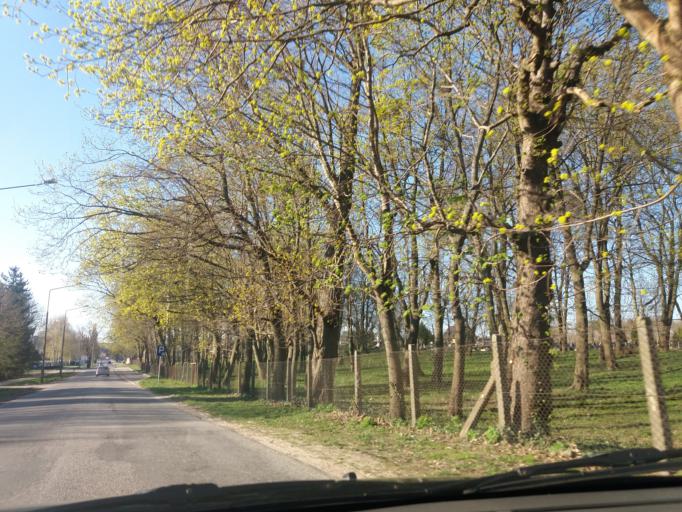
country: PL
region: Warmian-Masurian Voivodeship
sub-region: Powiat nidzicki
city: Nidzica
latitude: 53.3510
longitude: 20.4292
